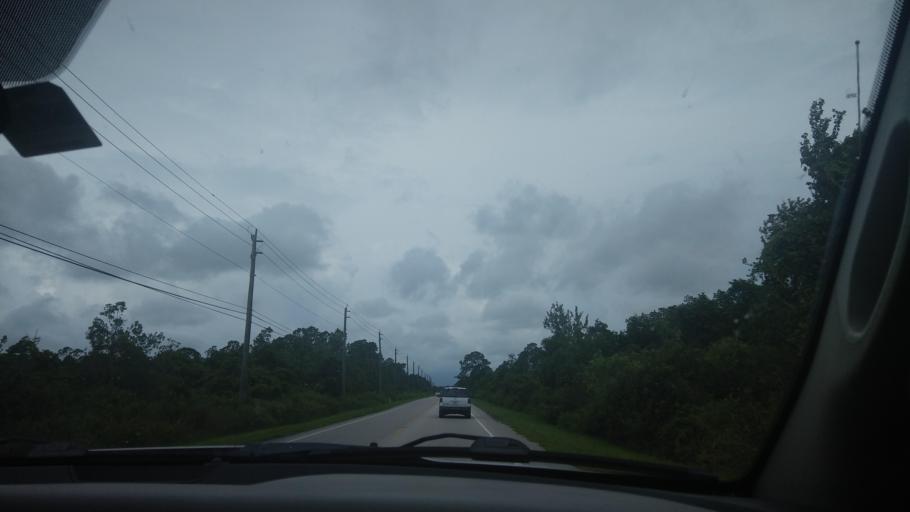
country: US
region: Florida
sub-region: Indian River County
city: Fellsmere
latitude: 27.7678
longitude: -80.5670
